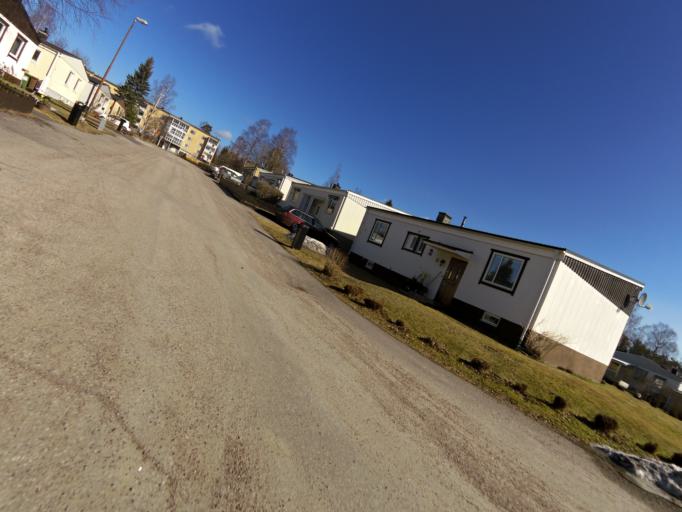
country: SE
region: Gaevleborg
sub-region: Hofors Kommun
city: Hofors
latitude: 60.5486
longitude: 16.2696
